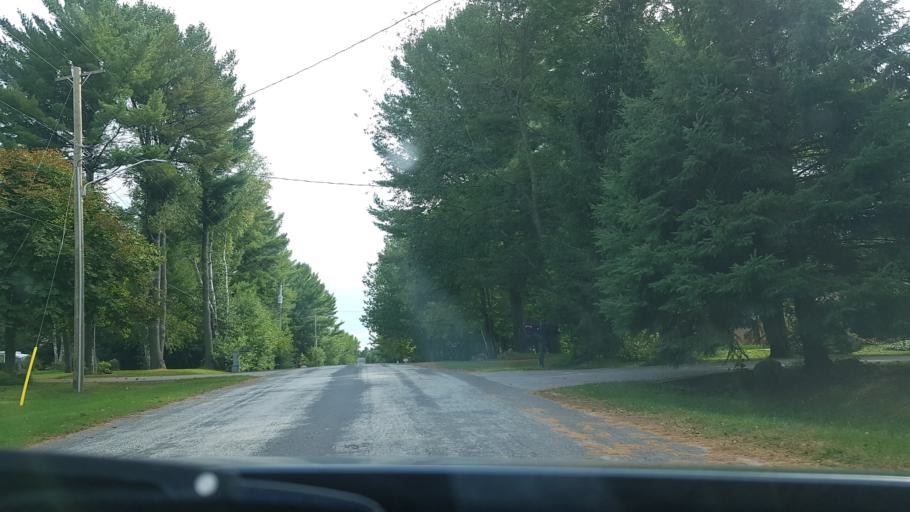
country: CA
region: Ontario
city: Barrie
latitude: 44.4841
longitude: -79.8195
